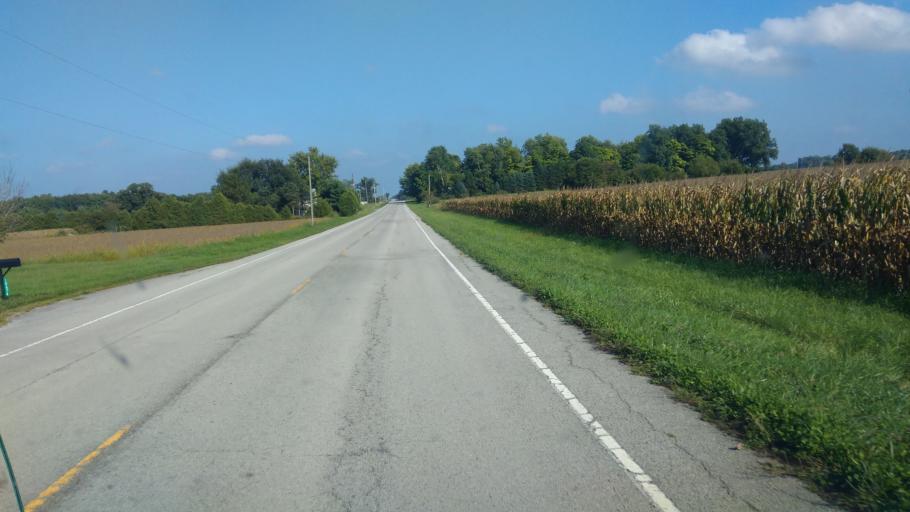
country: US
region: Ohio
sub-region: Hancock County
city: Arlington
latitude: 40.8341
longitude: -83.6770
